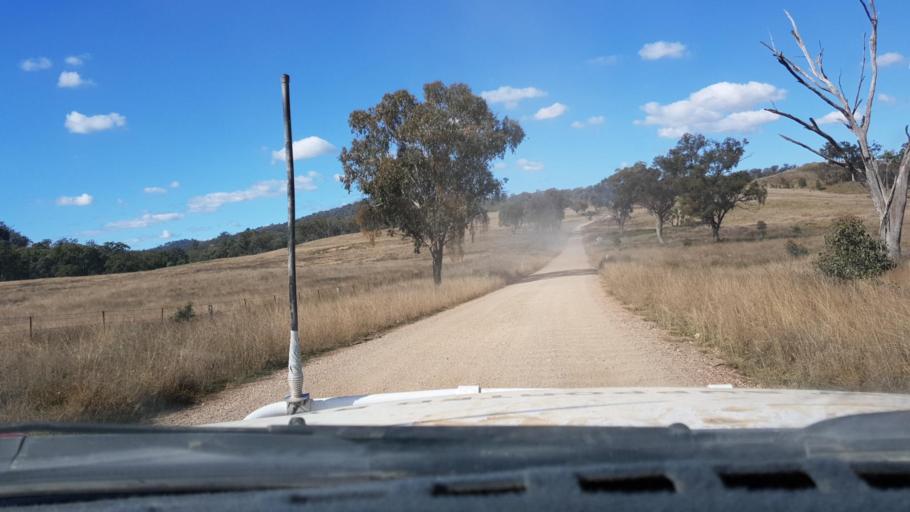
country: AU
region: New South Wales
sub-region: Tamworth Municipality
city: Manilla
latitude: -30.4533
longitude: 150.7381
